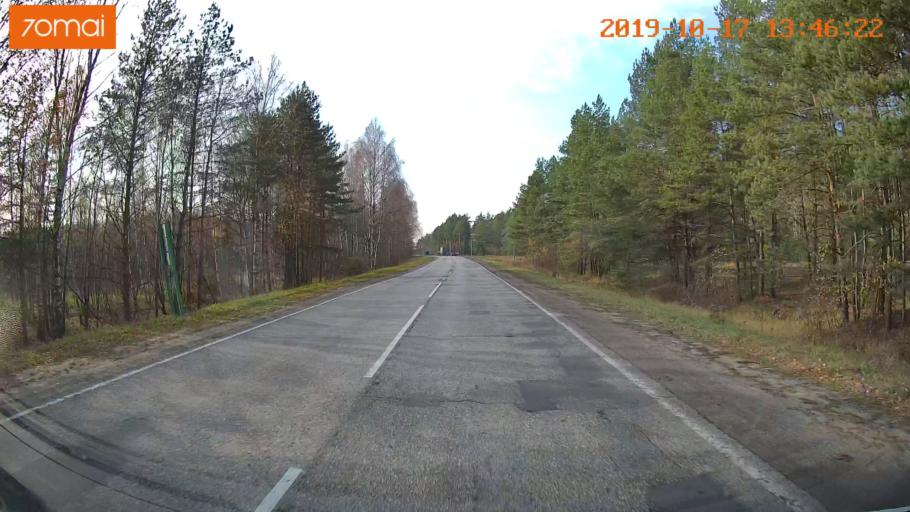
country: RU
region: Rjazan
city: Tuma
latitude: 55.1476
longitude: 40.4915
